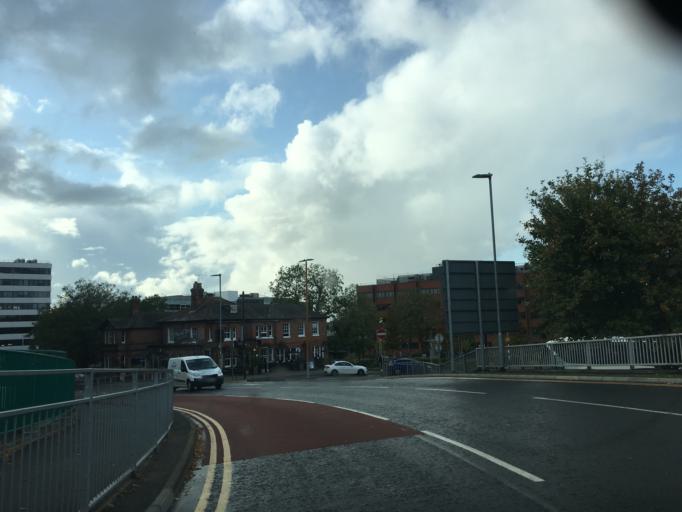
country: GB
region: England
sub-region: Bracknell Forest
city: Bracknell
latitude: 51.4131
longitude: -0.7506
